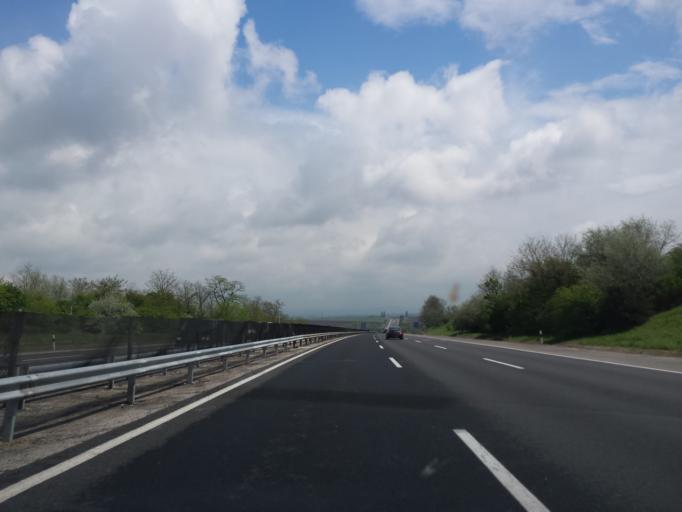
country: HU
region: Fejer
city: Many
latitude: 47.5109
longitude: 18.6528
